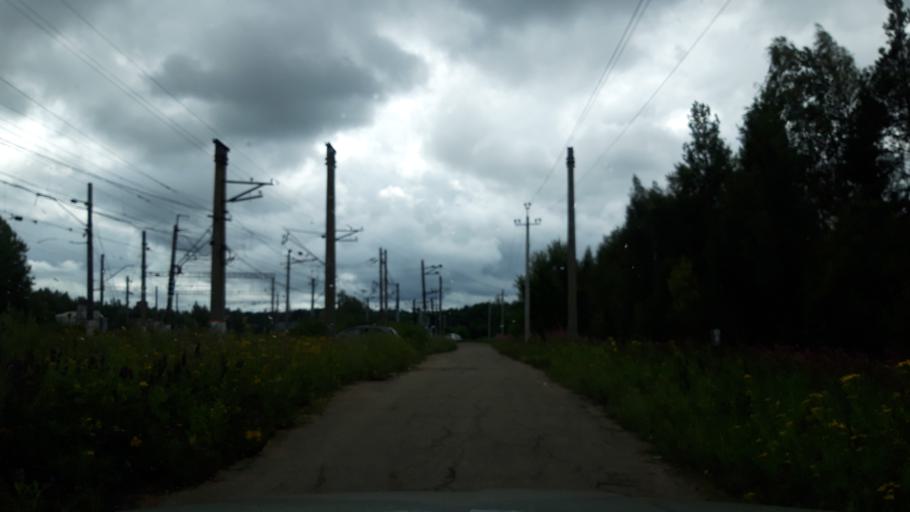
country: RU
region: Moskovskaya
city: Povarovo
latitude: 56.0394
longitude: 37.0537
